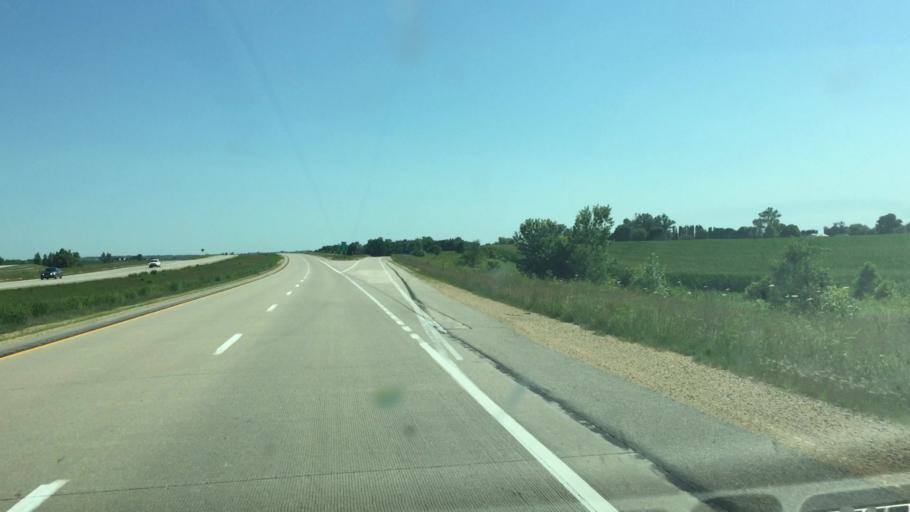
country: US
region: Iowa
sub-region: Jones County
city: Monticello
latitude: 42.2371
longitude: -91.1694
